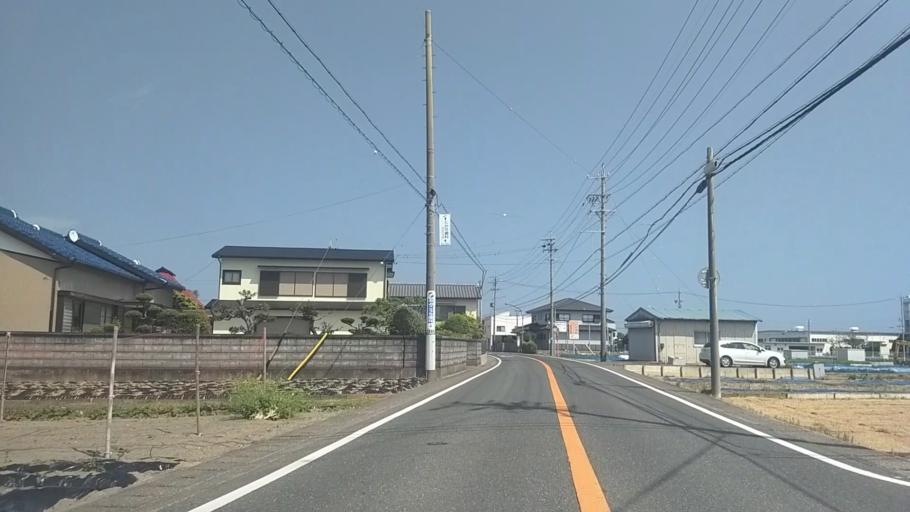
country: JP
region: Shizuoka
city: Hamamatsu
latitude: 34.6795
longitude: 137.7118
